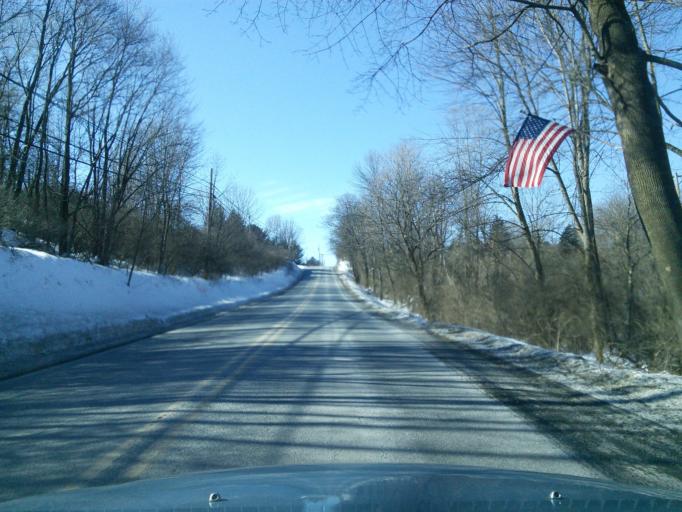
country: US
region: Pennsylvania
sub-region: Centre County
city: Bellefonte
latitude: 40.8972
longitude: -77.8064
